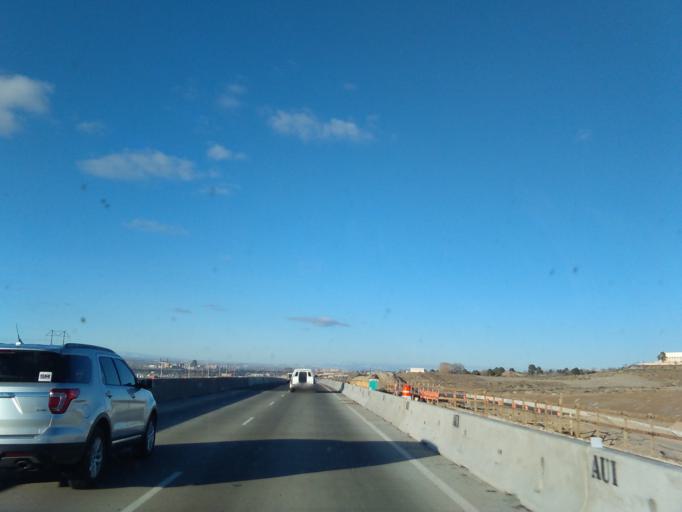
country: US
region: New Mexico
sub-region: Bernalillo County
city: South Valley
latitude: 35.0235
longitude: -106.6383
